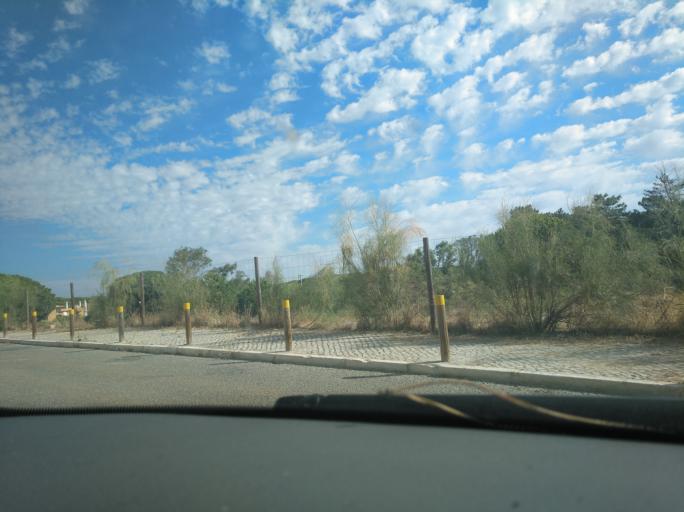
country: PT
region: Faro
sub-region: Vila Real de Santo Antonio
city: Monte Gordo
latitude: 37.1766
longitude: -7.4793
